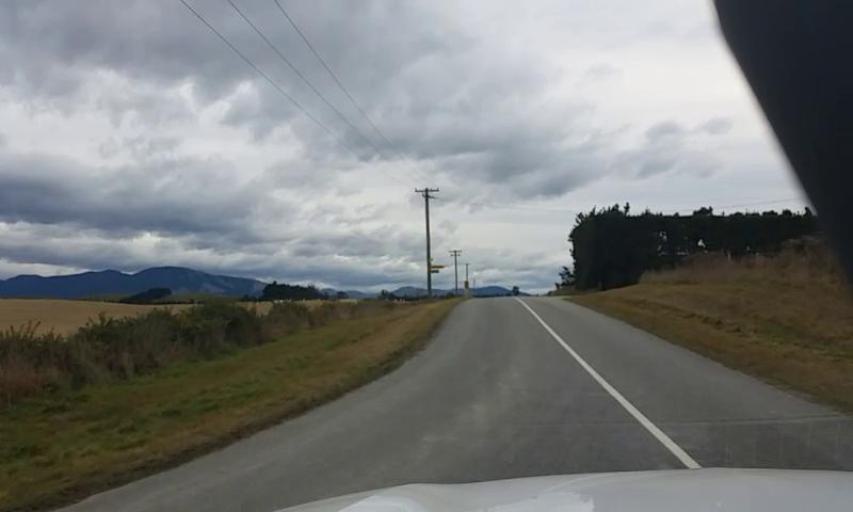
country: NZ
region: Canterbury
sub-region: Waimakariri District
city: Kaiapoi
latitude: -43.2917
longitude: 172.4374
